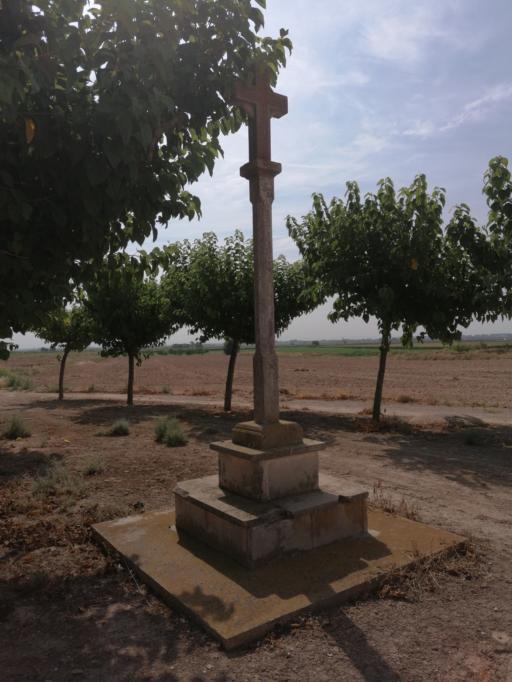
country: ES
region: Catalonia
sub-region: Provincia de Lleida
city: Bellvis
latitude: 41.6945
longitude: 0.8340
